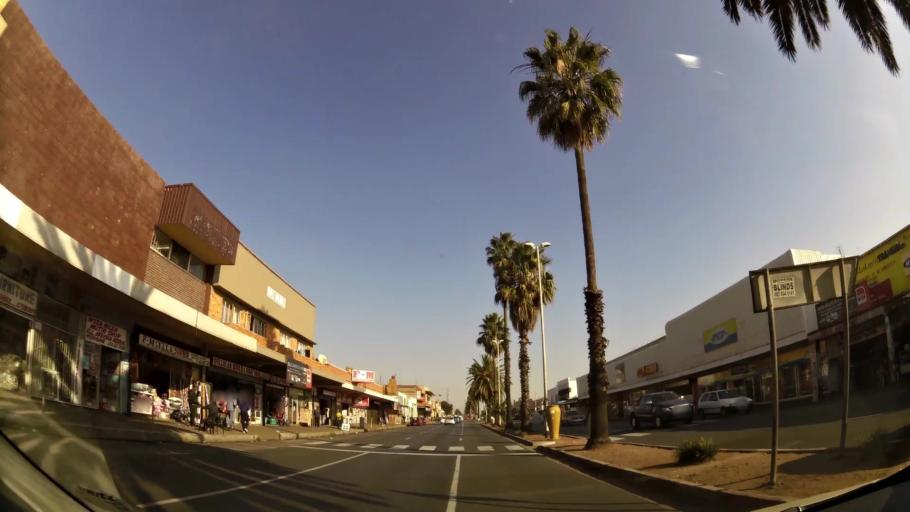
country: ZA
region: Gauteng
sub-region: West Rand District Municipality
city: Randfontein
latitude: -26.1813
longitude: 27.7040
